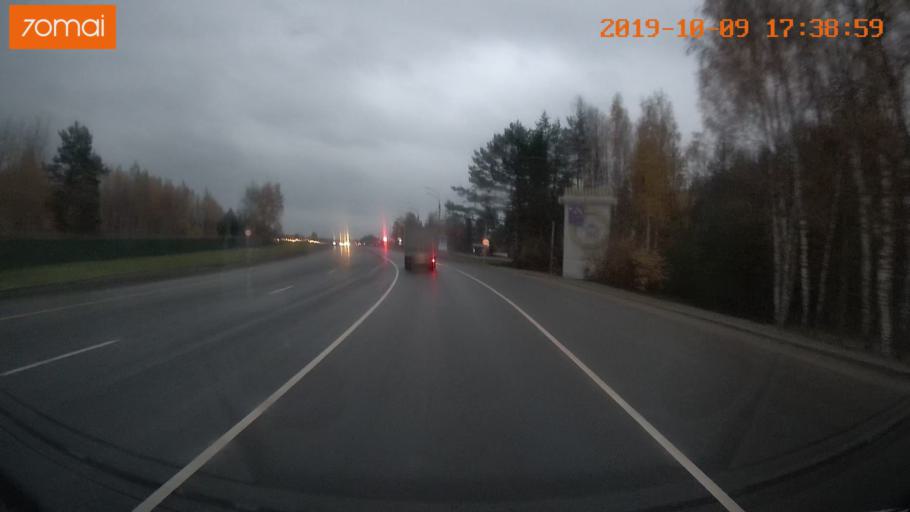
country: RU
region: Ivanovo
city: Bogorodskoye
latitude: 57.0648
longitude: 40.9533
